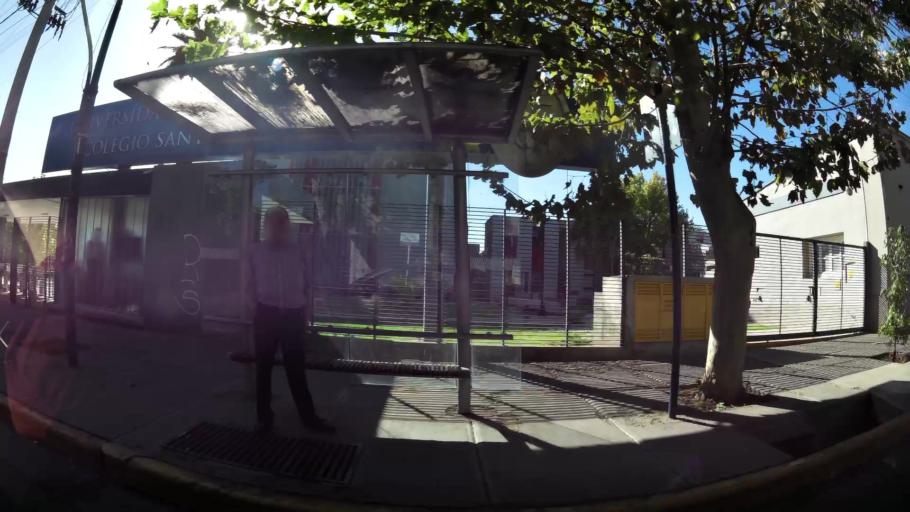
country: AR
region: Mendoza
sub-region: Departamento de Godoy Cruz
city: Godoy Cruz
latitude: -32.9169
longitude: -68.8428
